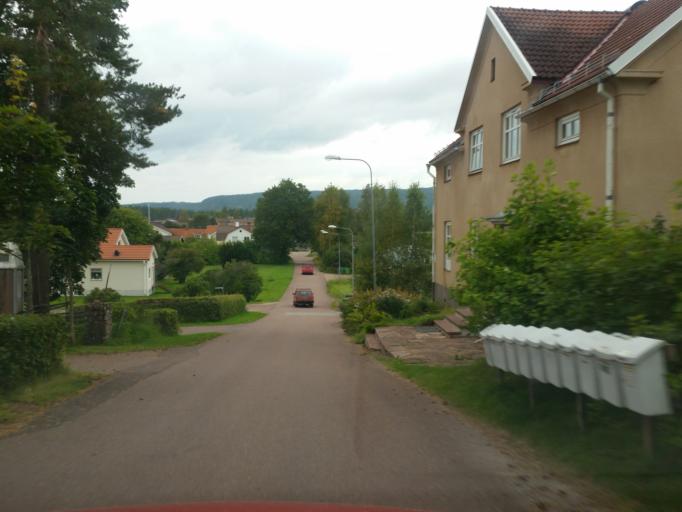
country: SE
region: Dalarna
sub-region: Leksand Municipality
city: Smedby
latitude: 60.6761
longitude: 15.0989
